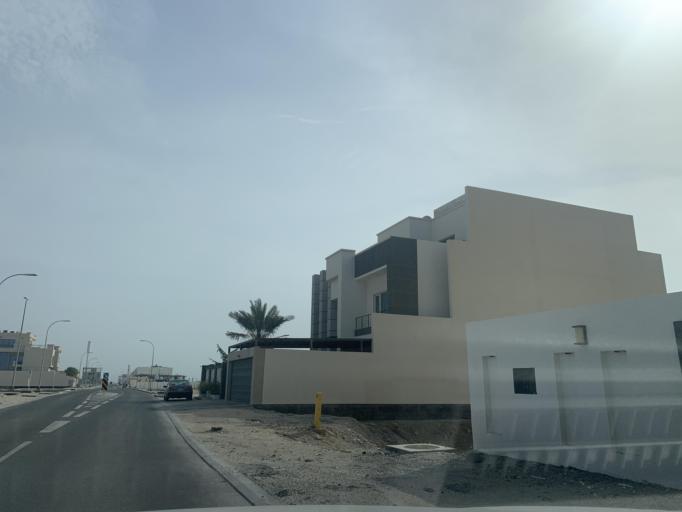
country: BH
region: Muharraq
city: Al Muharraq
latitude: 26.3221
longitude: 50.6238
